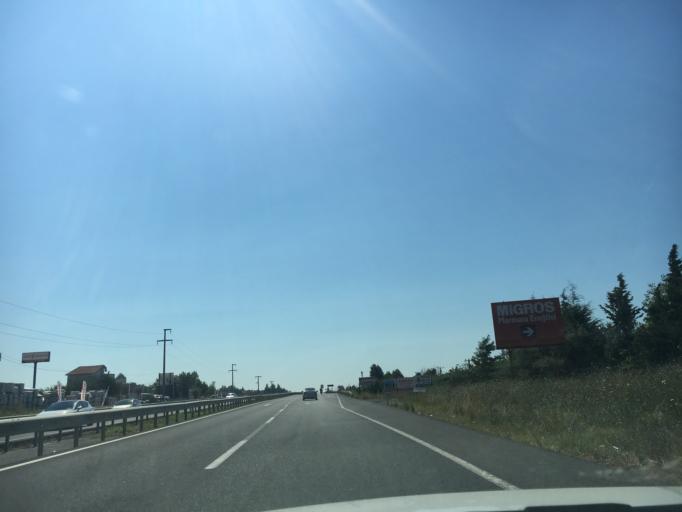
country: TR
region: Tekirdag
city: Marmara Ereglisi
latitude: 40.9760
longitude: 27.8743
